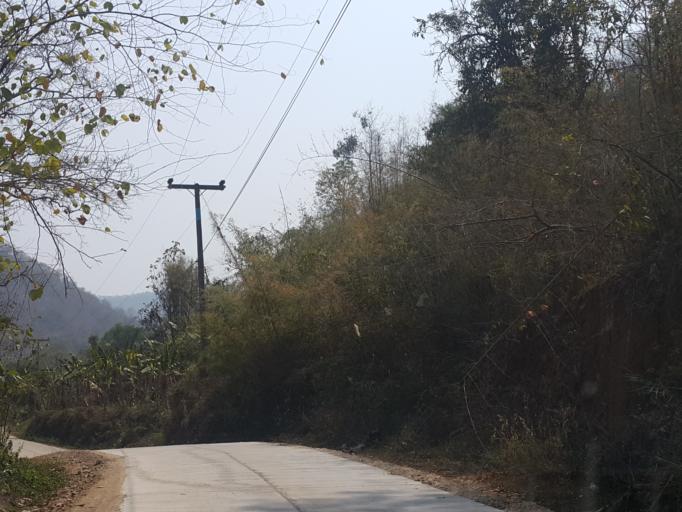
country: TH
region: Chiang Mai
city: Hang Dong
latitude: 18.7420
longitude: 98.8251
